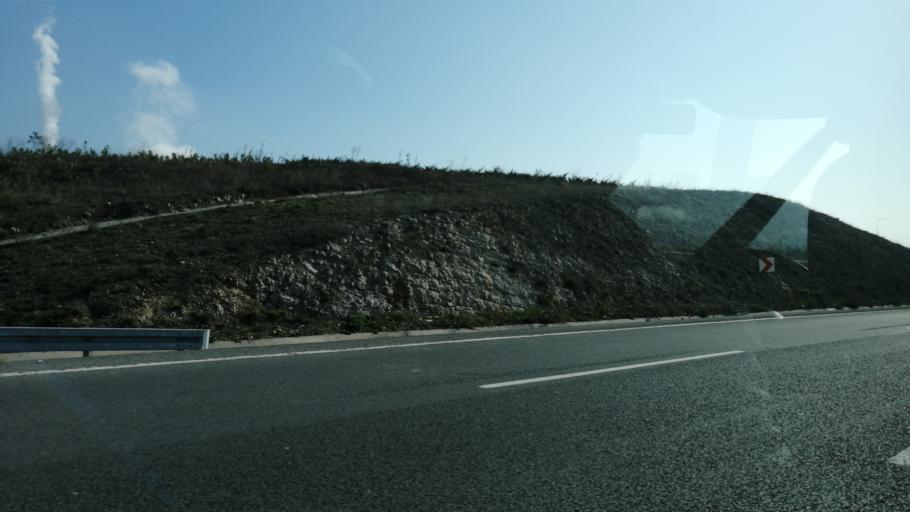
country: TR
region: Kocaeli
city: Tavsanli
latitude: 40.7987
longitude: 29.5077
